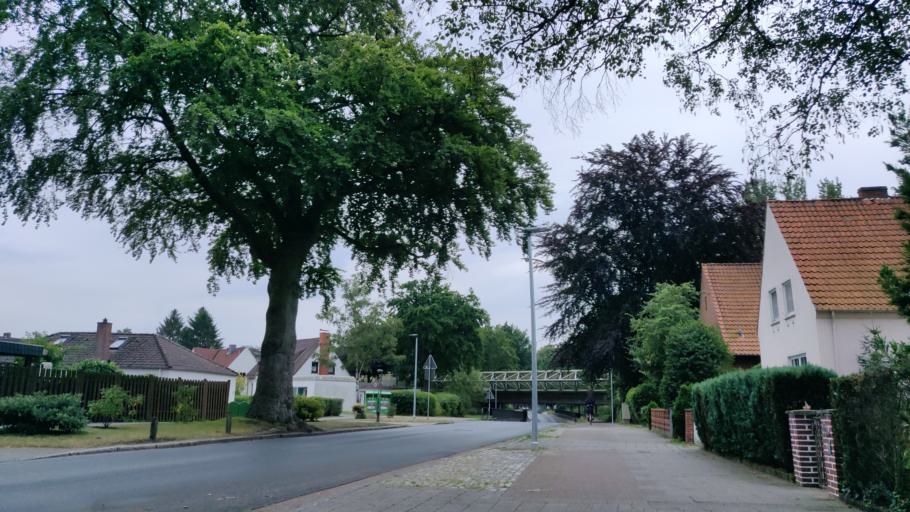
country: DE
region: Lower Saxony
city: Lilienthal
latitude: 53.0957
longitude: 8.8964
